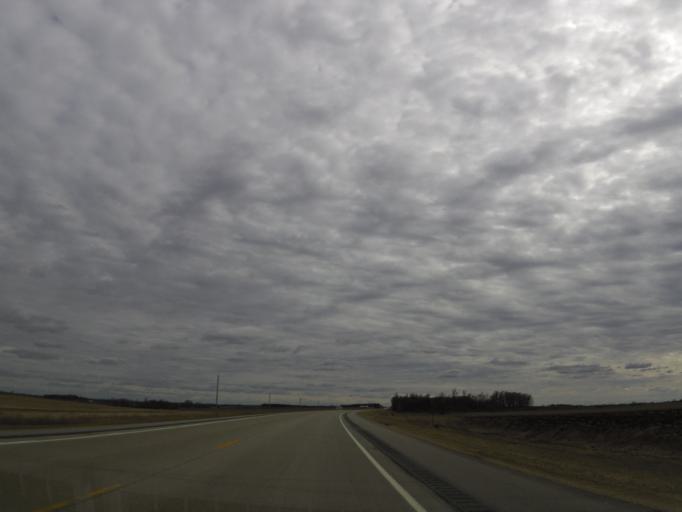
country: US
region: Minnesota
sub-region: Fillmore County
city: Spring Valley
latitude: 43.5397
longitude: -92.3695
